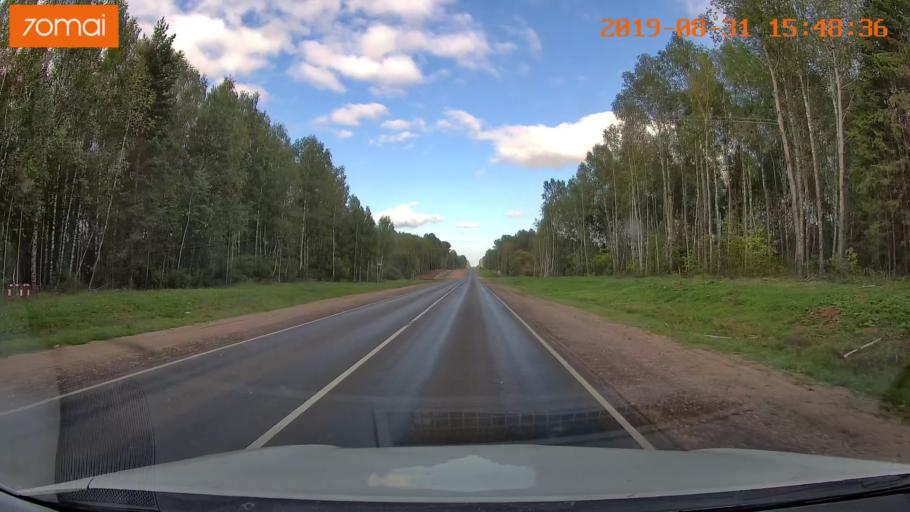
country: RU
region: Kaluga
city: Yukhnov
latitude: 54.6865
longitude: 35.0339
